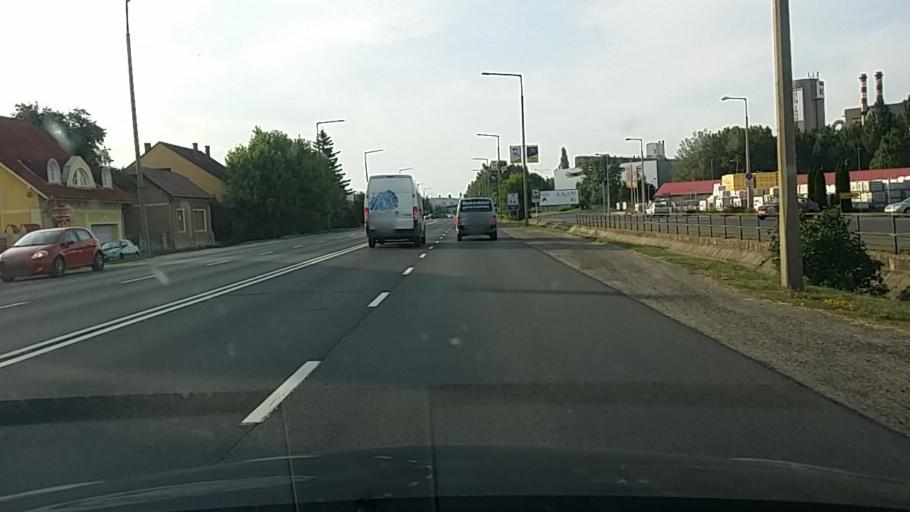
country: HU
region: Borsod-Abauj-Zemplen
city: Miskolc
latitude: 48.0593
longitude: 20.7961
